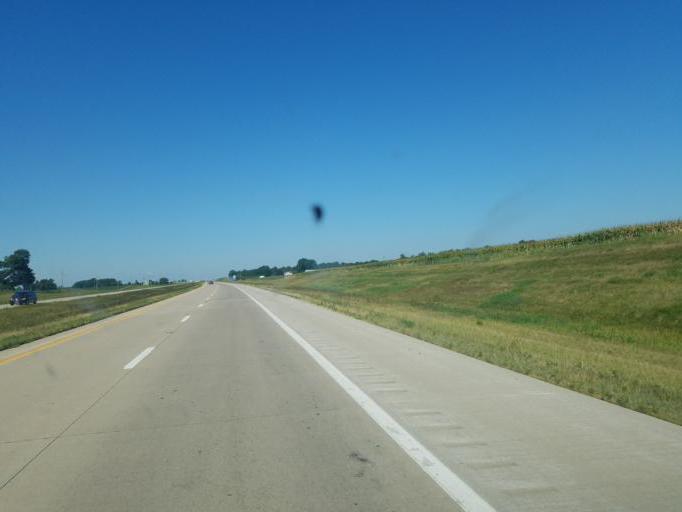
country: US
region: Ohio
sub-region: Wyandot County
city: Upper Sandusky
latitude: 40.8080
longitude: -83.1519
